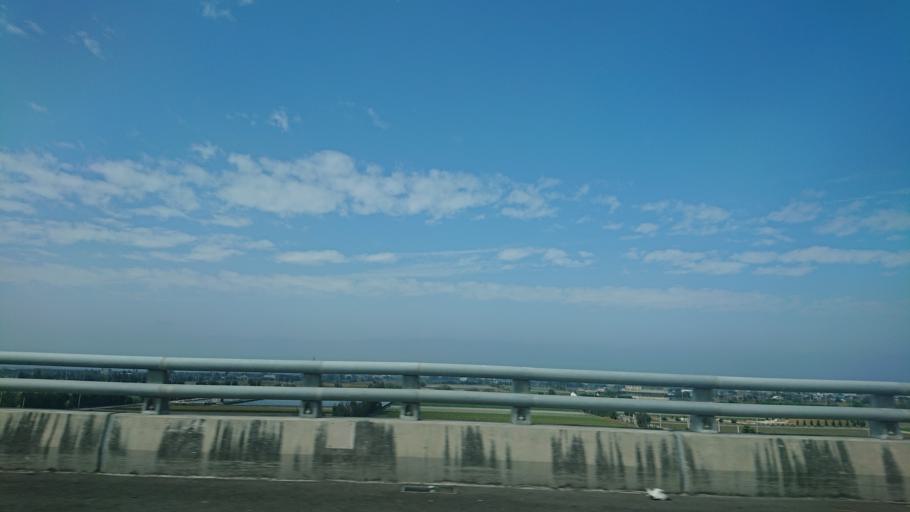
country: TW
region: Taiwan
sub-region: Yunlin
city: Douliu
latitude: 23.8413
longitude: 120.2925
